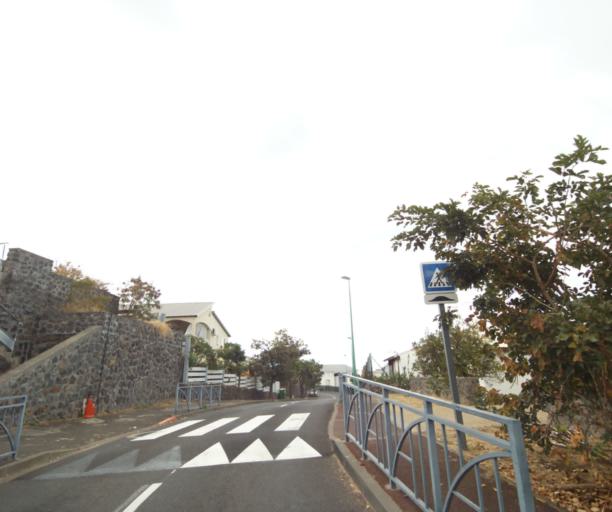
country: RE
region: Reunion
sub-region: Reunion
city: Saint-Paul
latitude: -21.0613
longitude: 55.2300
